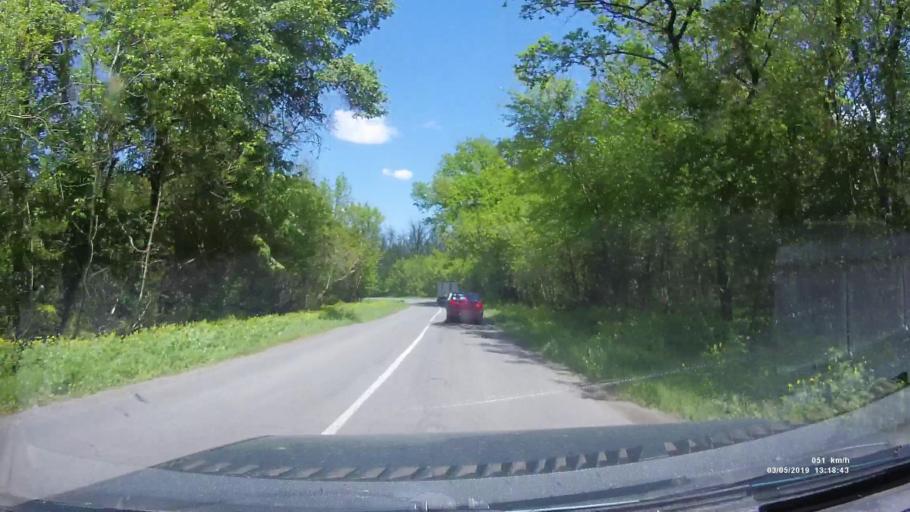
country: RU
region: Rostov
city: Semikarakorsk
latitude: 47.5342
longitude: 40.7506
